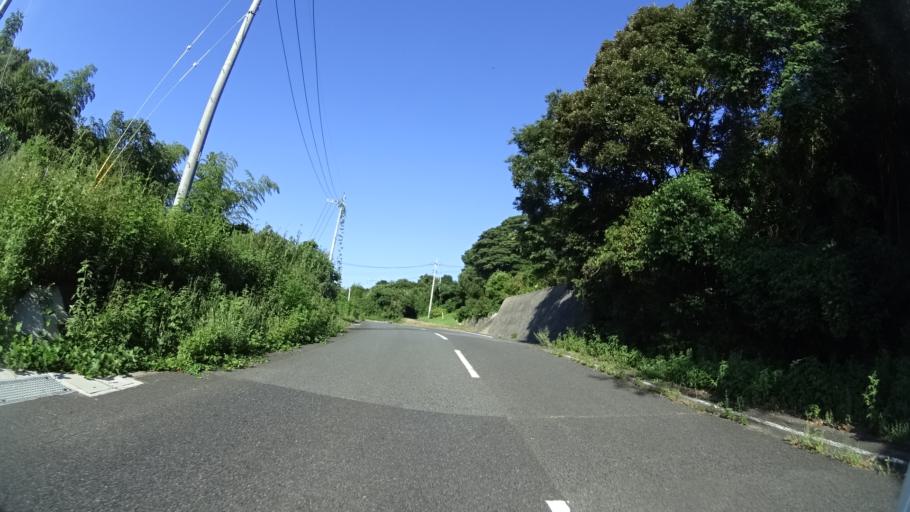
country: JP
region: Yamaguchi
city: Nagato
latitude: 34.3416
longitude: 130.9012
